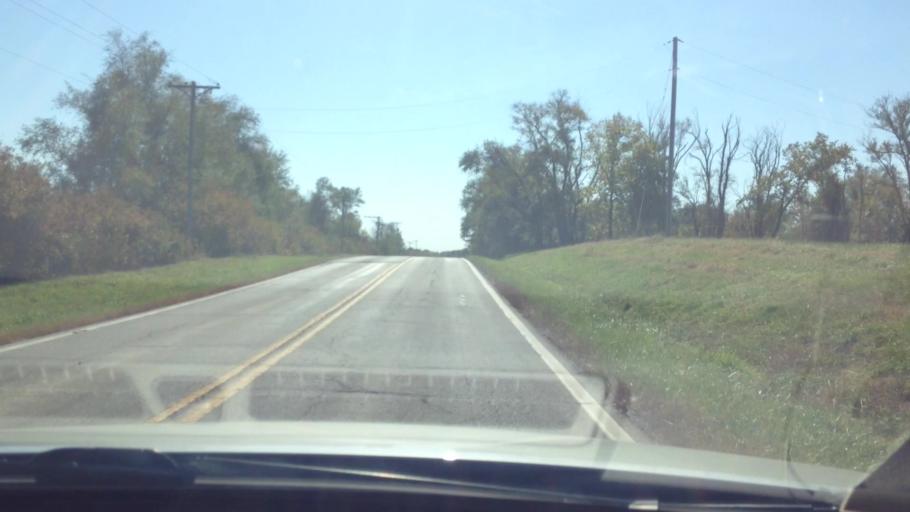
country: US
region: Missouri
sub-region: Clay County
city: Smithville
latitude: 39.3274
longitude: -94.6488
